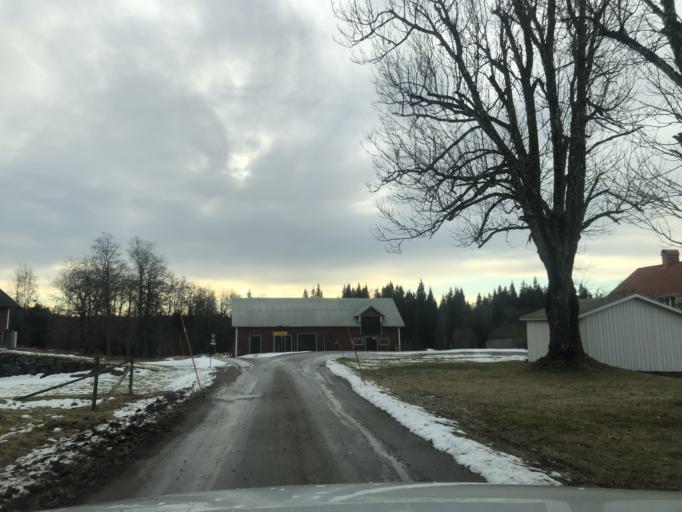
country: SE
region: Vaestra Goetaland
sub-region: Ulricehamns Kommun
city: Ulricehamn
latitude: 57.7936
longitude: 13.4869
